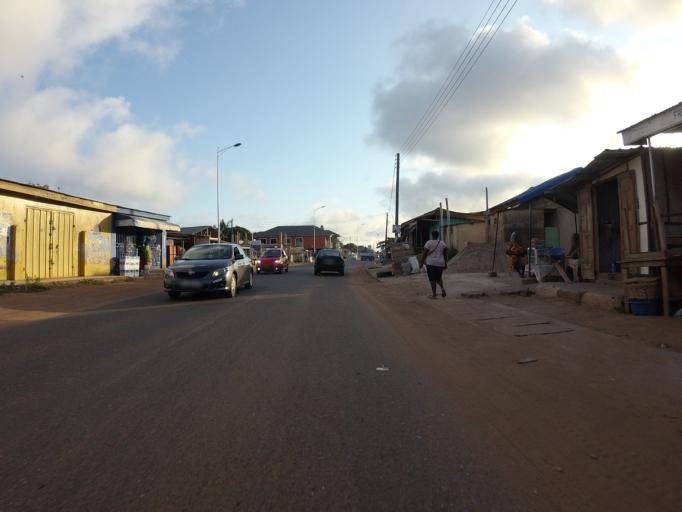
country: GH
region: Greater Accra
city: Teshi Old Town
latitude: 5.5960
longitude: -0.1266
